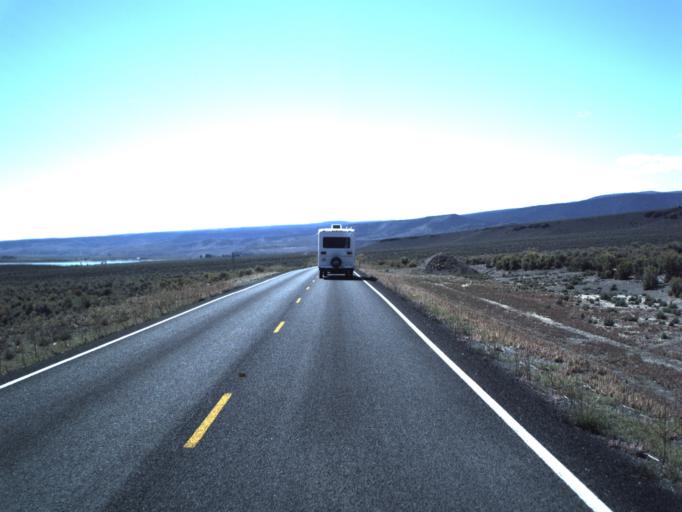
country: US
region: Utah
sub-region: Piute County
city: Junction
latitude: 38.2014
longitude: -112.0078
